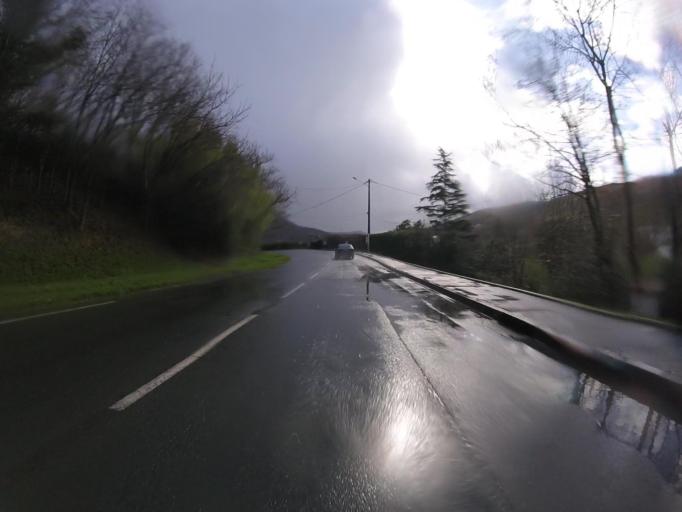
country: FR
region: Aquitaine
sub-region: Departement des Pyrenees-Atlantiques
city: Ascain
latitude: 43.3424
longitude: -1.6342
